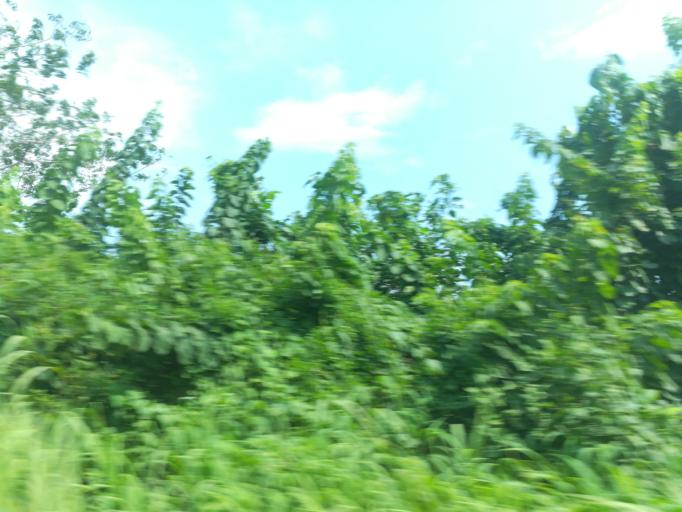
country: NG
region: Lagos
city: Ikorodu
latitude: 6.6130
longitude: 3.6428
